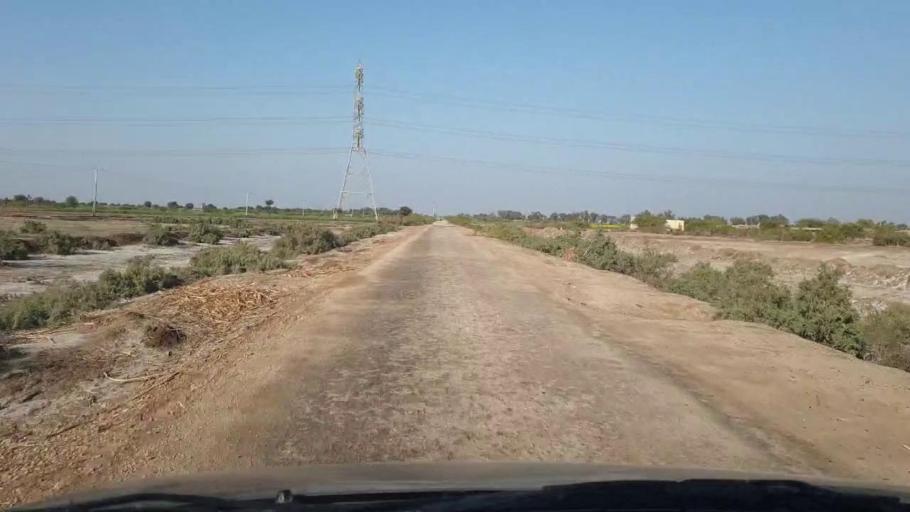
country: PK
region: Sindh
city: Samaro
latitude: 25.1516
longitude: 69.3096
